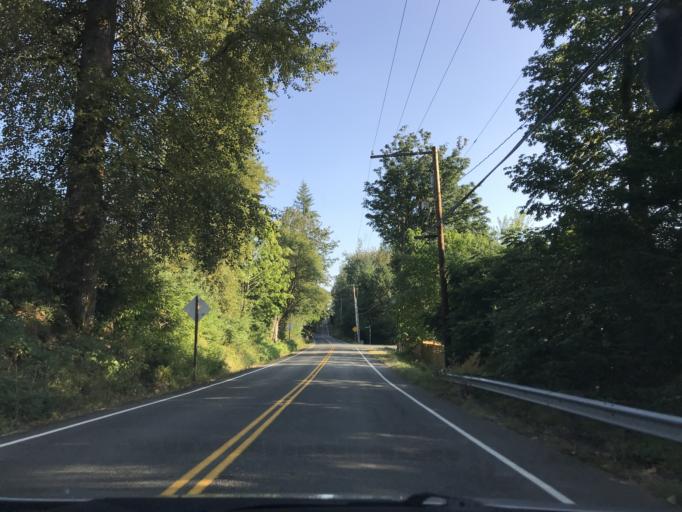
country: US
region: Washington
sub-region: King County
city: Maple Valley
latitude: 47.4009
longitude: -122.0164
